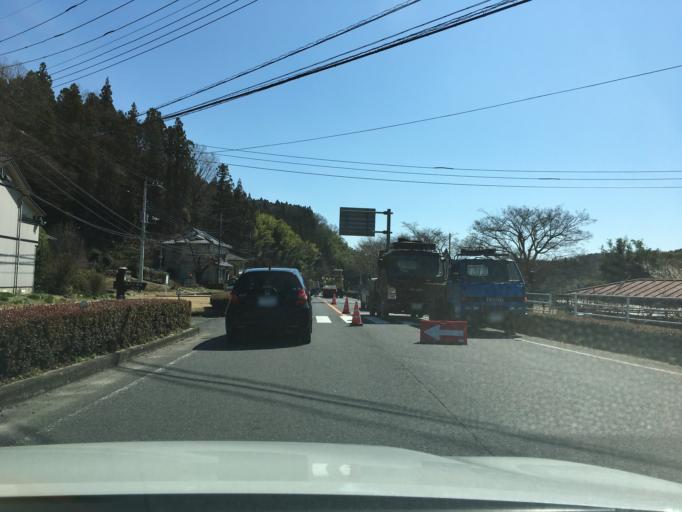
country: JP
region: Tochigi
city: Kuroiso
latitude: 37.0361
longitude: 140.1723
